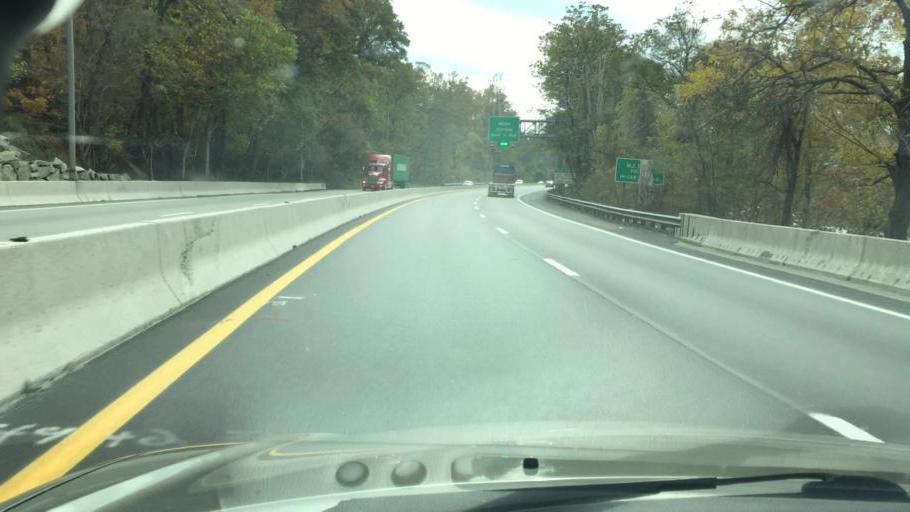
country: US
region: Pennsylvania
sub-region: Monroe County
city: East Stroudsburg
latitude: 40.9660
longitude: -75.1183
